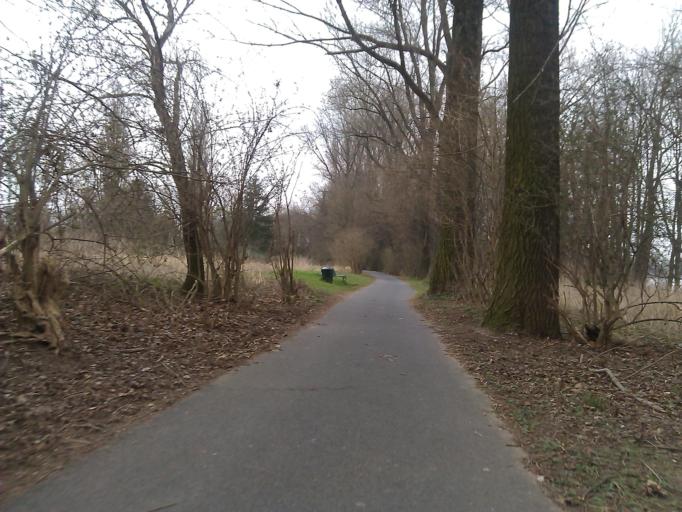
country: DE
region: North Rhine-Westphalia
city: Wesseling
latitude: 50.8578
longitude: 7.0070
